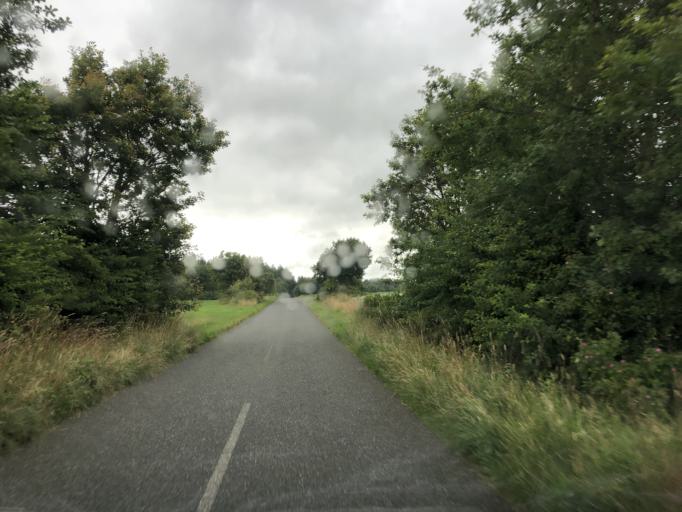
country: DK
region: Central Jutland
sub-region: Herning Kommune
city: Vildbjerg
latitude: 56.2059
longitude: 8.8340
